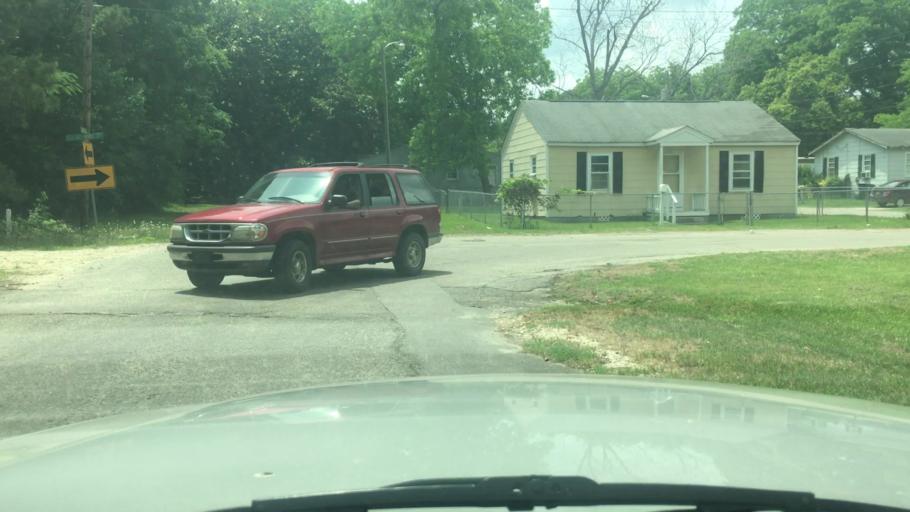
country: US
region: North Carolina
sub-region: Cumberland County
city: Fort Bragg
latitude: 35.0904
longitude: -78.9562
